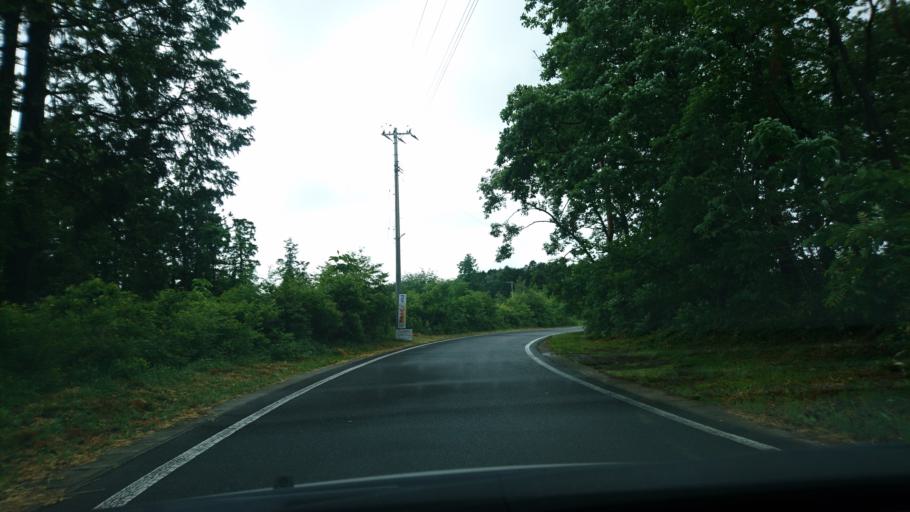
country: JP
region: Iwate
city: Ichinoseki
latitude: 38.9026
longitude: 141.1424
